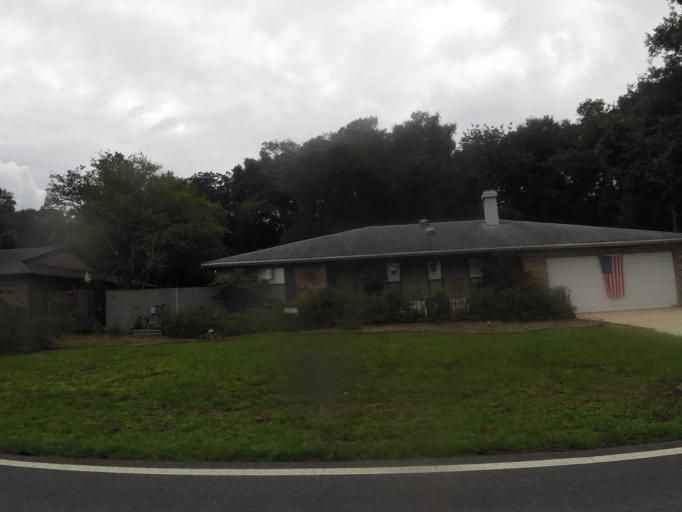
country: US
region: Florida
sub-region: Duval County
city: Jacksonville Beach
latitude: 30.2839
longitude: -81.4339
